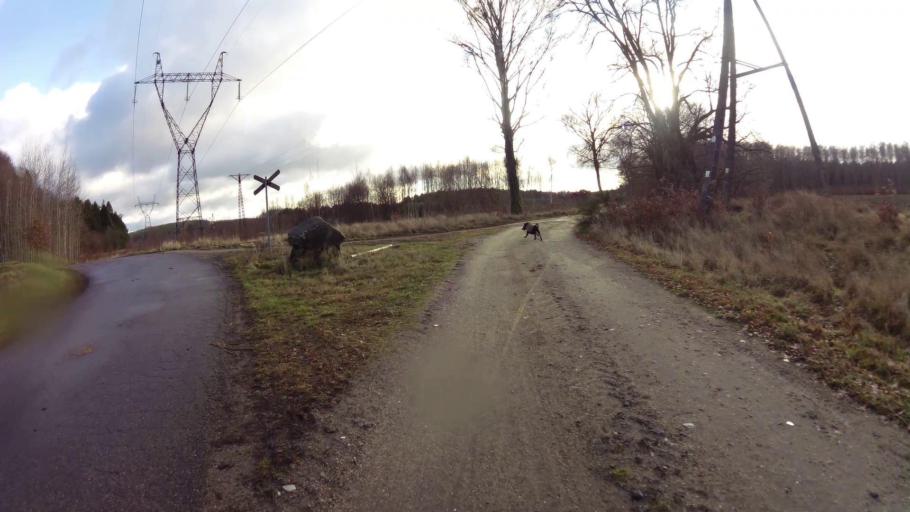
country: PL
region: West Pomeranian Voivodeship
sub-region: Powiat koszalinski
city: Sianow
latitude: 54.1227
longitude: 16.2986
